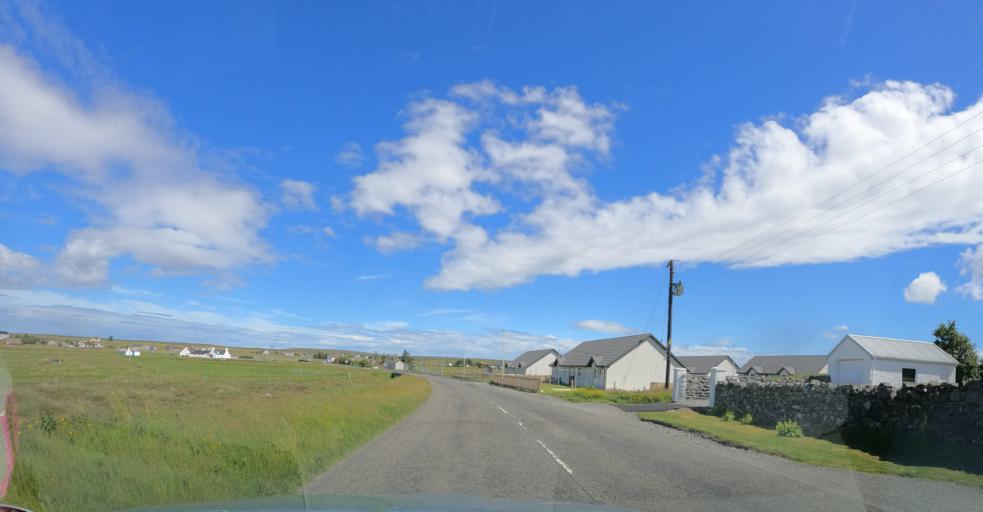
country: GB
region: Scotland
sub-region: Eilean Siar
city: Isle of Lewis
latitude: 58.3486
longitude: -6.5237
